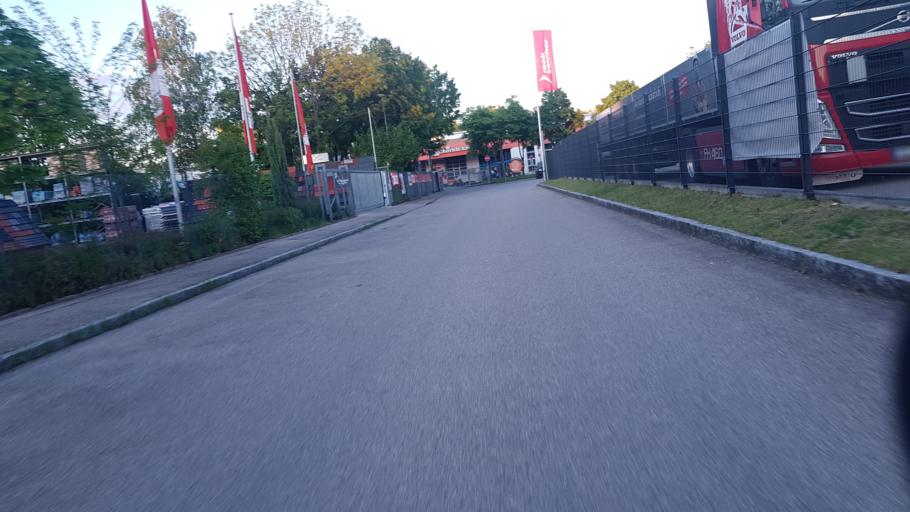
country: DE
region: Bavaria
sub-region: Upper Bavaria
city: Bogenhausen
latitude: 48.1376
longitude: 11.6628
